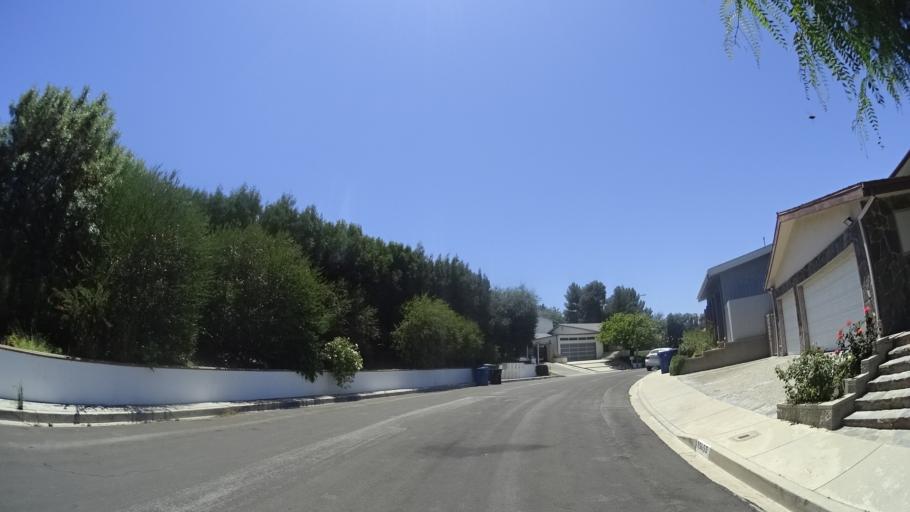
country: US
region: California
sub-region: Los Angeles County
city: Sherman Oaks
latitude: 34.1325
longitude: -118.4747
